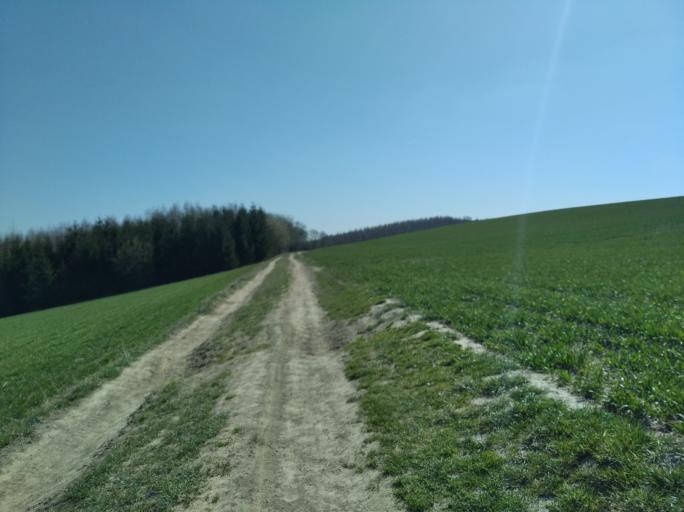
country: PL
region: Subcarpathian Voivodeship
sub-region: Powiat strzyzowski
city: Polomia
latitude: 49.8833
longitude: 21.8532
